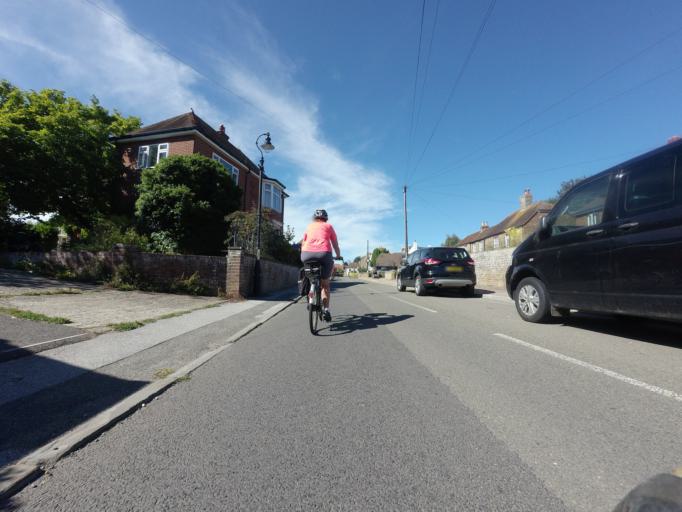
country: GB
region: England
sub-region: Kent
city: Birchington-on-Sea
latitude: 51.3320
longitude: 1.3153
